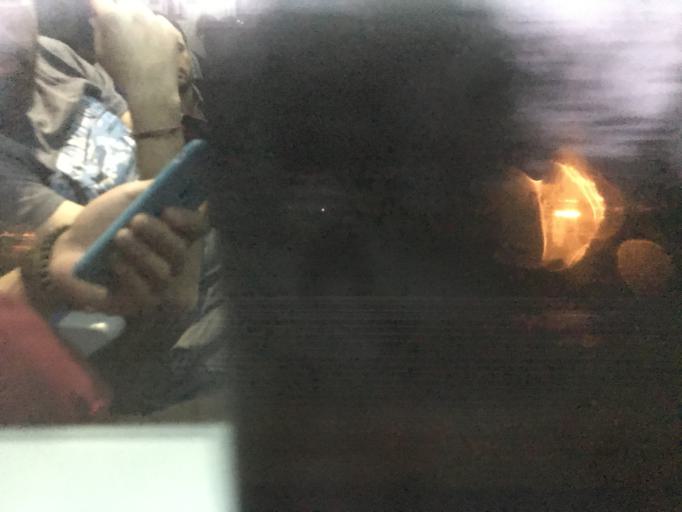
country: TR
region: Kocaeli
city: Korfez
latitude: 40.7475
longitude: 29.7893
